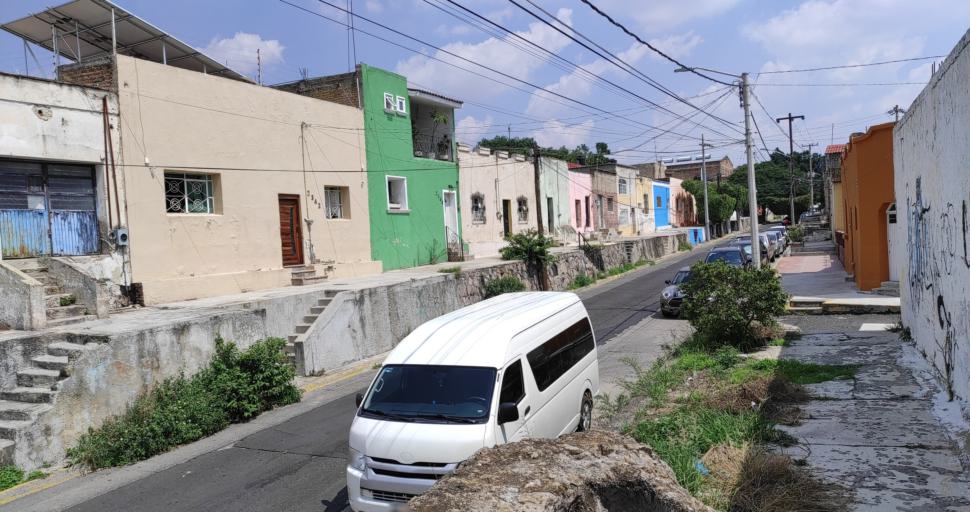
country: MX
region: Jalisco
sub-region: Zapopan
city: Zapopan
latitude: 20.7115
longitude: -103.3547
